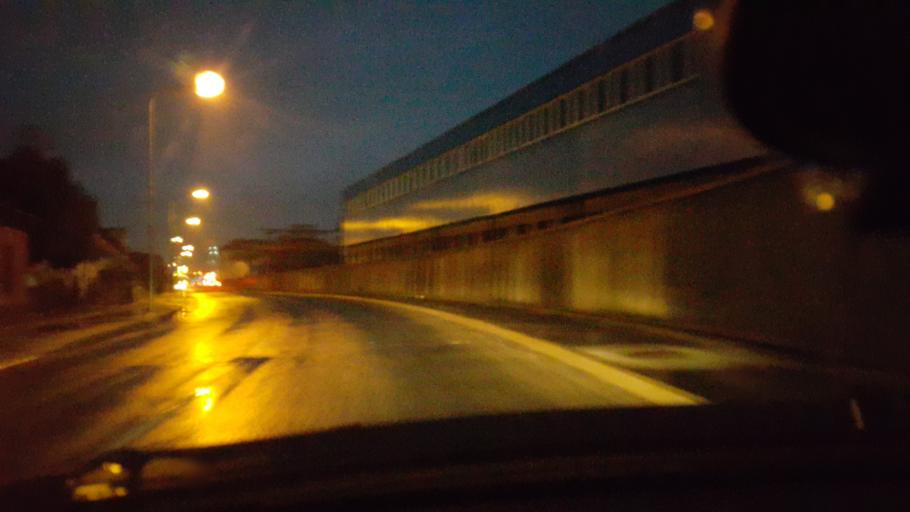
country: SI
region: Maribor
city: Maribor
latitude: 46.5362
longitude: 15.6551
